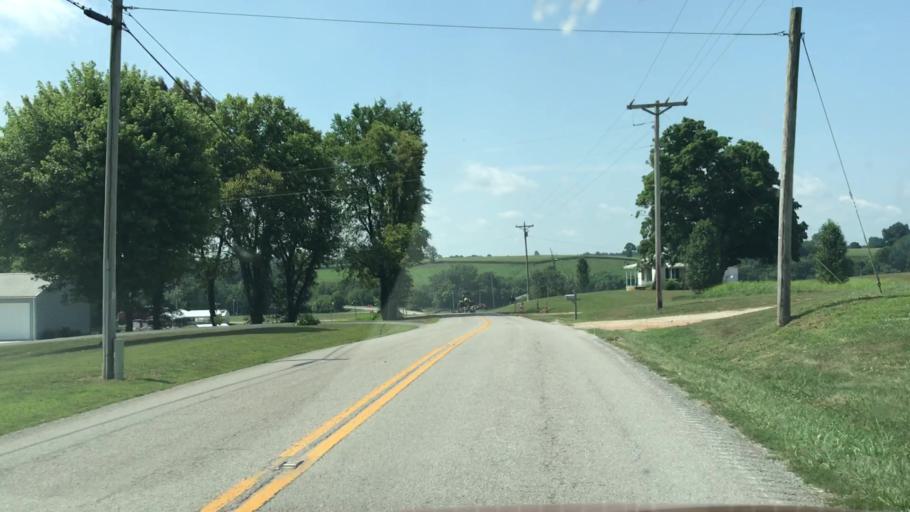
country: US
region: Kentucky
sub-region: Barren County
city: Glasgow
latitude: 36.8704
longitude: -85.8488
